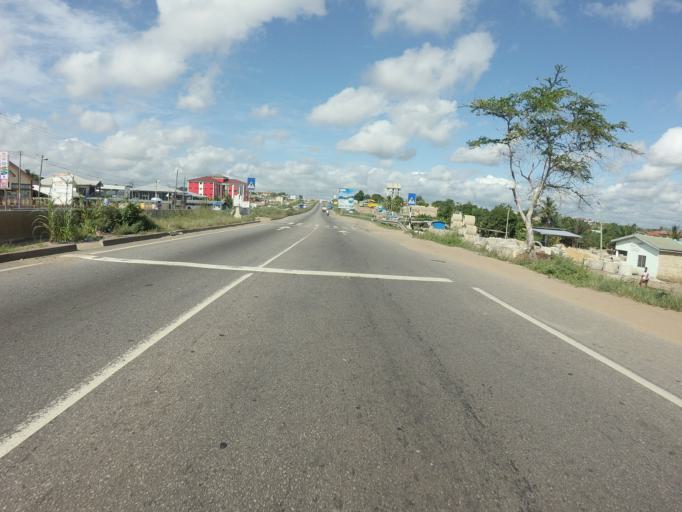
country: GH
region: Central
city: Kasoa
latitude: 5.5314
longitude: -0.4430
